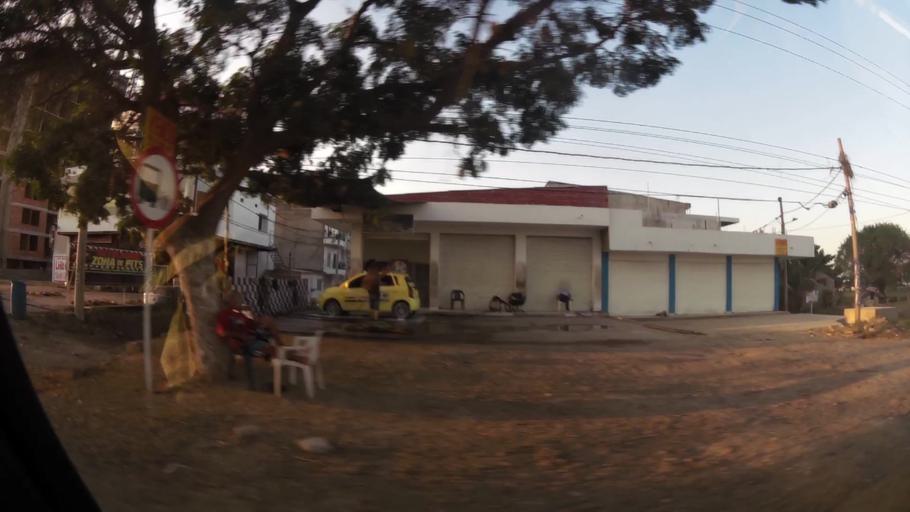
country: CO
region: Bolivar
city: Cartagena
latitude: 10.3990
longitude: -75.4694
